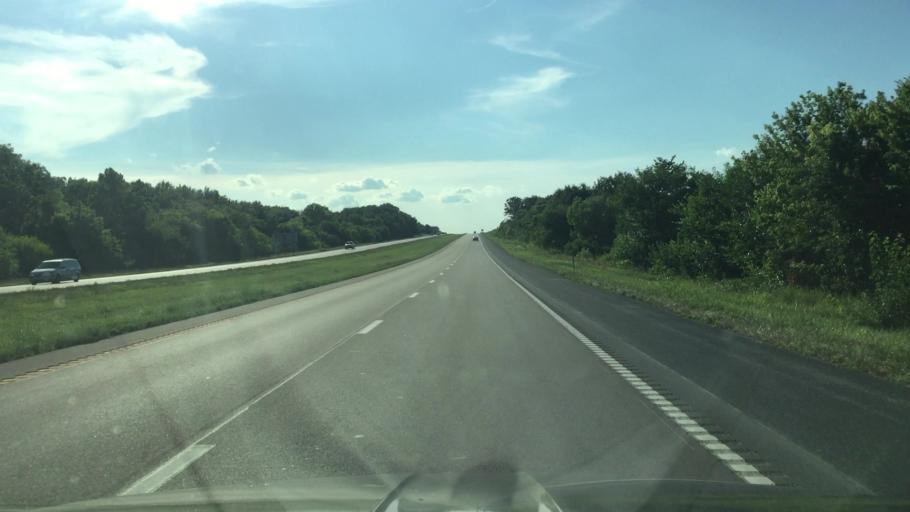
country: US
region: Missouri
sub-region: Pettis County
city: La Monte
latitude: 38.7424
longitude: -93.3267
